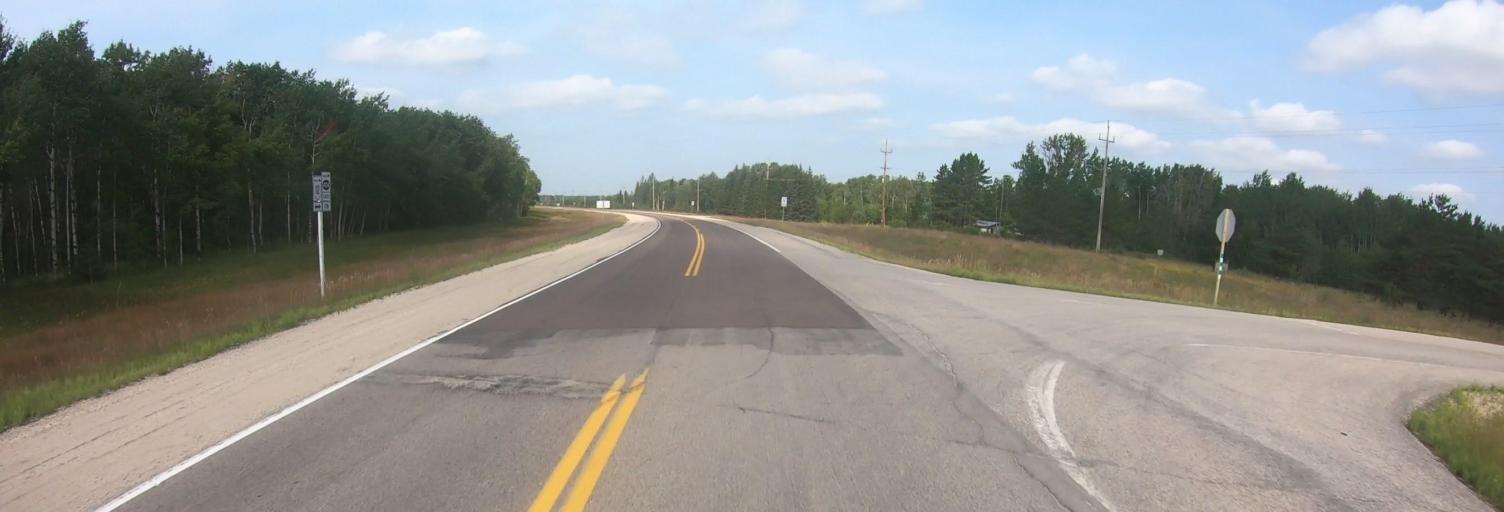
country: CA
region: Manitoba
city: La Broquerie
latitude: 49.2666
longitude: -96.3681
